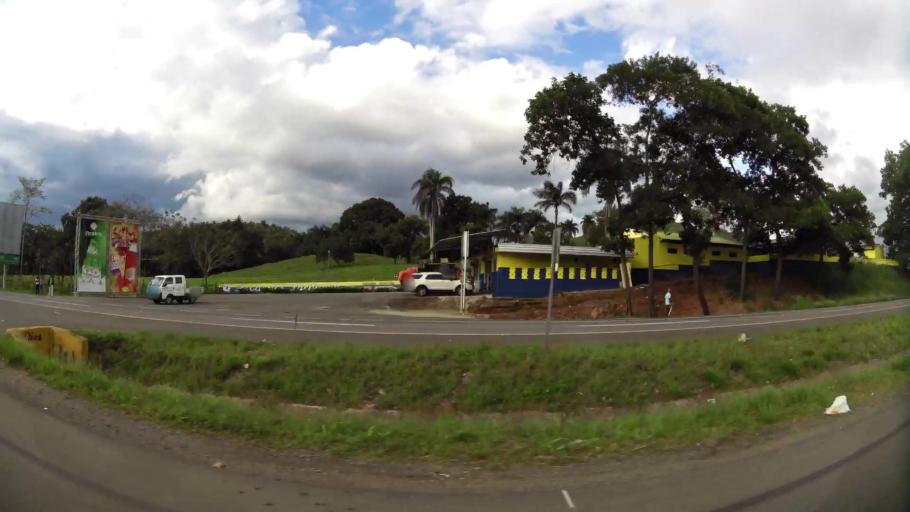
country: DO
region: Monsenor Nouel
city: Piedra Blanca
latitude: 18.8559
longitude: -70.3375
